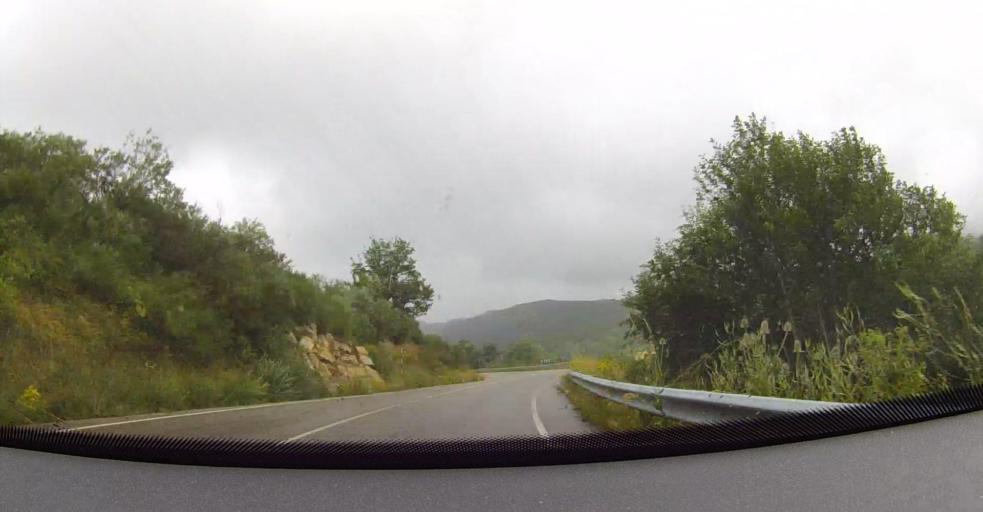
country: ES
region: Castille and Leon
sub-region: Provincia de Leon
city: Marana
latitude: 43.0724
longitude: -5.1956
